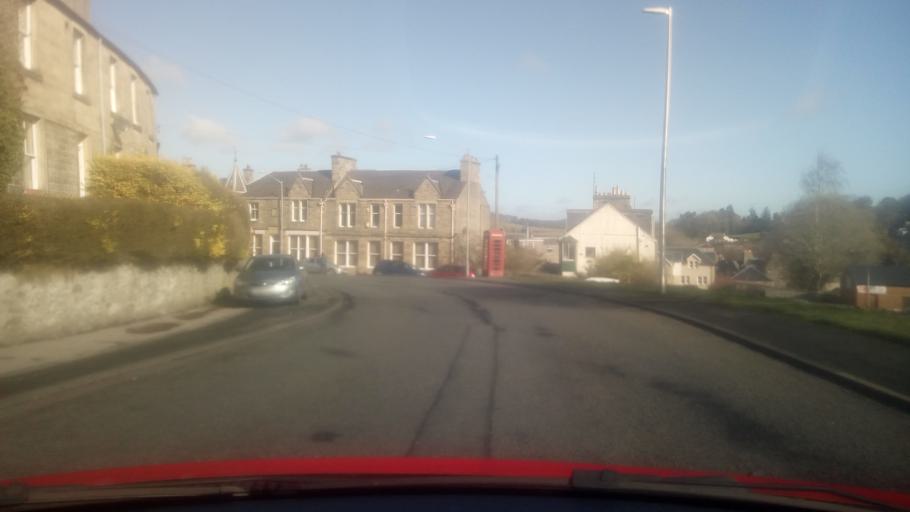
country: GB
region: Scotland
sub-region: The Scottish Borders
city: Selkirk
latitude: 55.5470
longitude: -2.8479
